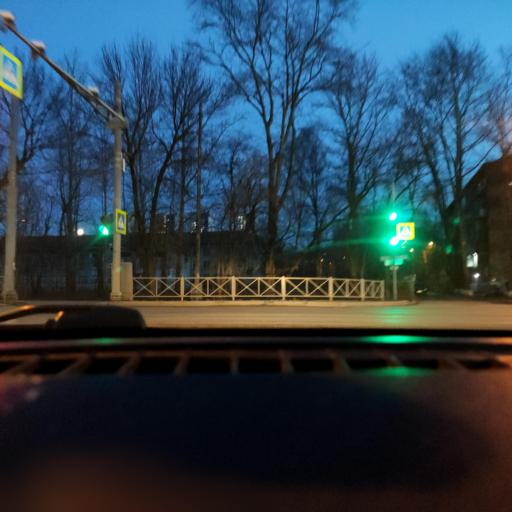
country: RU
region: Perm
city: Kondratovo
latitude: 57.9743
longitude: 56.1592
